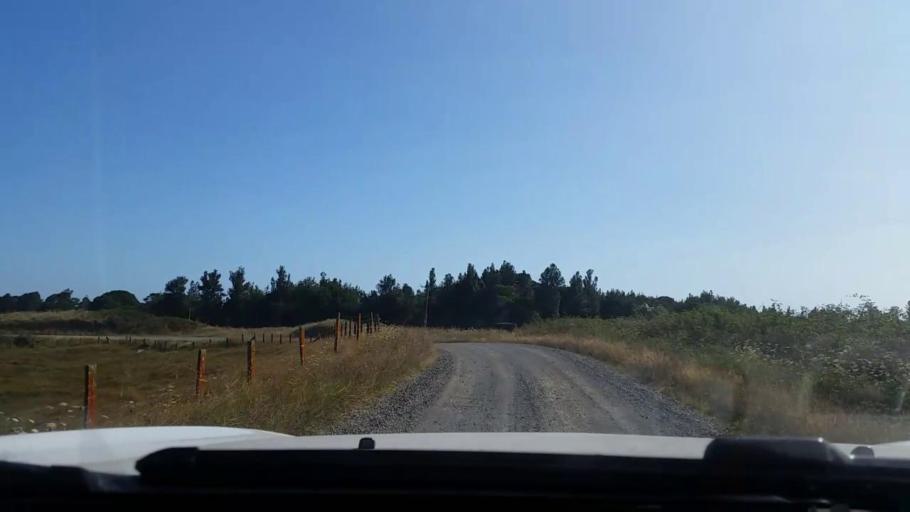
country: NZ
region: Bay of Plenty
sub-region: Western Bay of Plenty District
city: Maketu
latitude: -37.9694
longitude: 176.4357
